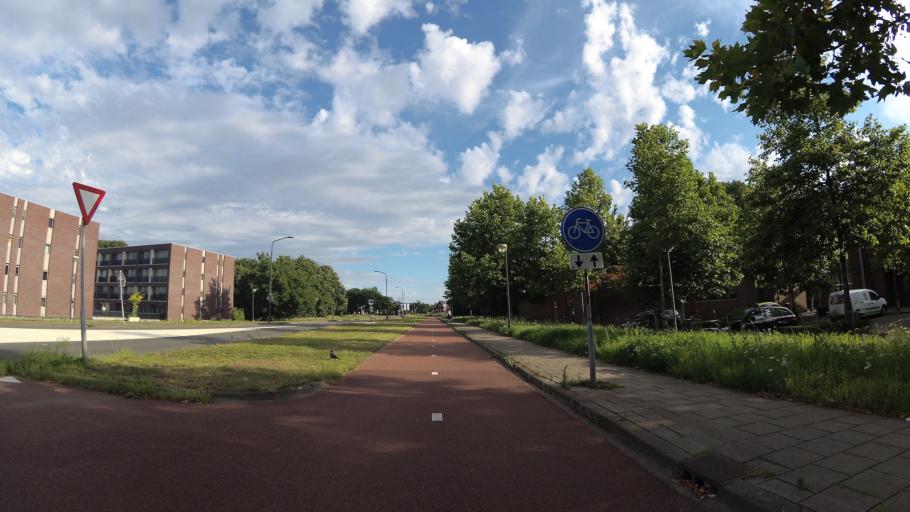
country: NL
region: North Brabant
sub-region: Gemeente Oosterhout
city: Oosterhout
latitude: 51.6469
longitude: 4.8334
